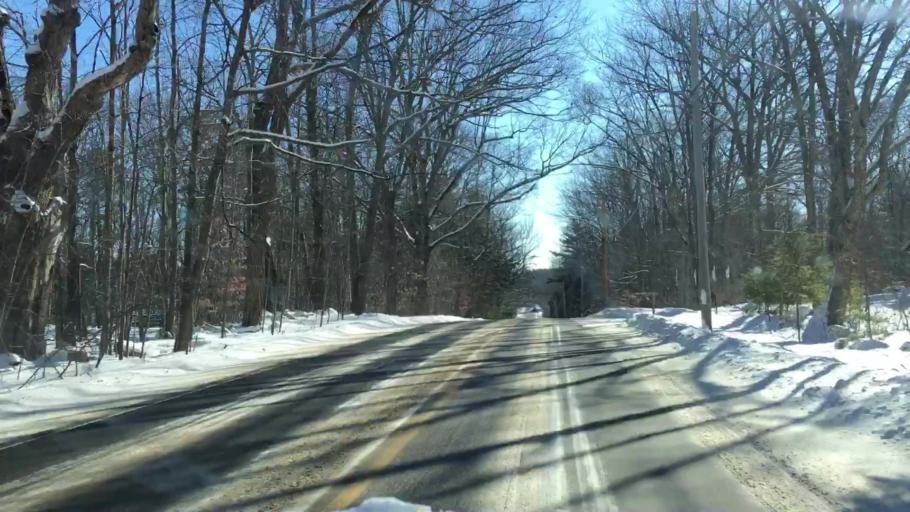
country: US
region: Maine
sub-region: Androscoggin County
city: Lisbon Falls
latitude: 43.9383
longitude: -70.0661
